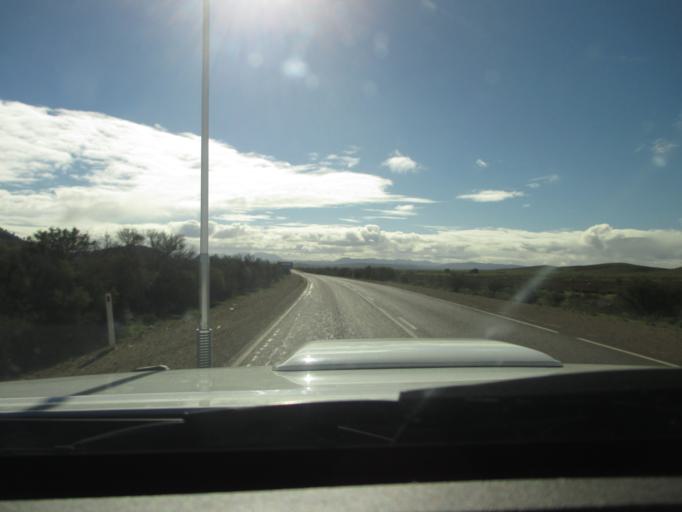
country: AU
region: South Australia
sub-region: Flinders Ranges
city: Quorn
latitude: -31.9248
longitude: 138.4222
